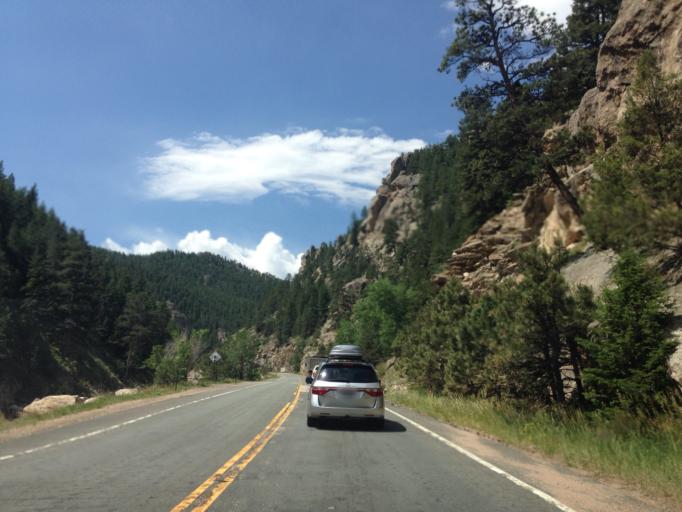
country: US
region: Colorado
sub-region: Larimer County
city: Estes Park
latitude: 40.4150
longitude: -105.3752
